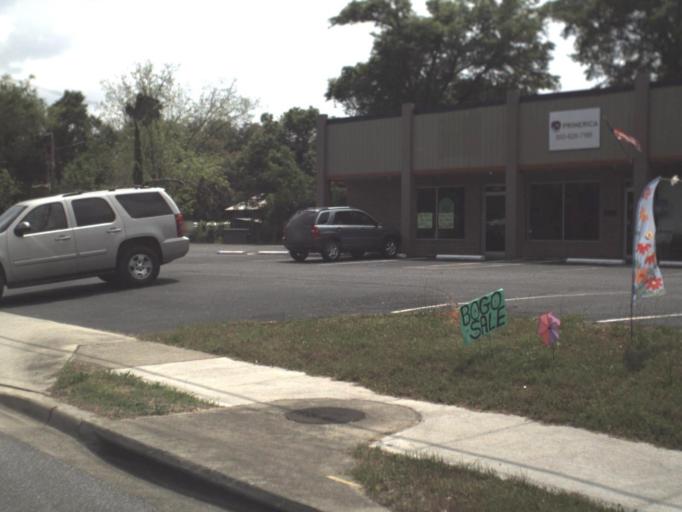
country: US
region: Florida
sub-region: Santa Rosa County
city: Milton
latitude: 30.6242
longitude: -87.0568
